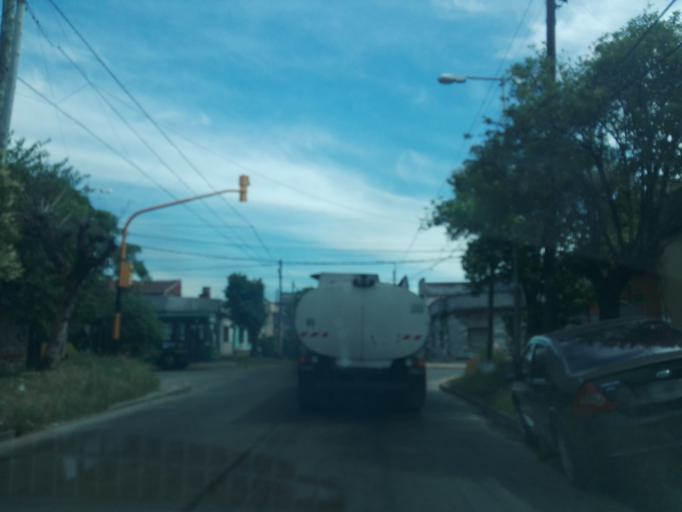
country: AR
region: Buenos Aires
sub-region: Partido de Avellaneda
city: Avellaneda
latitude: -34.6896
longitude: -58.3525
